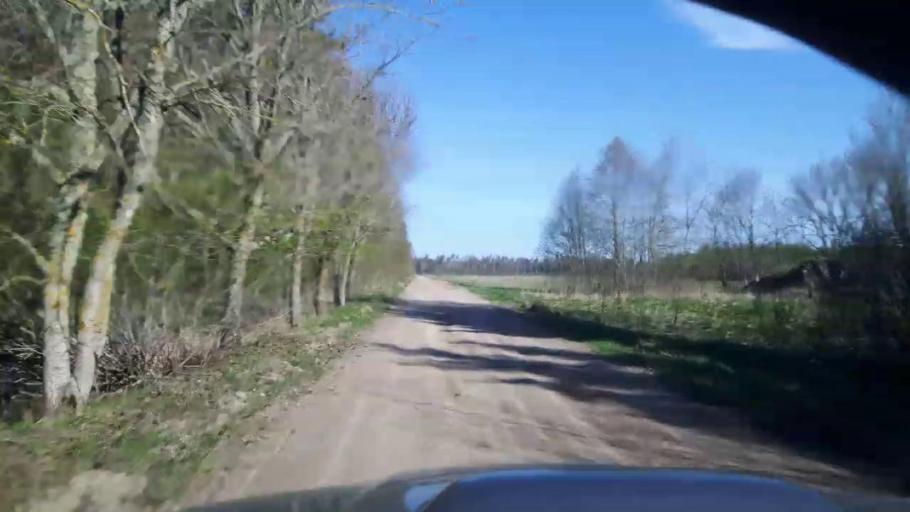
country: EE
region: Paernumaa
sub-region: Tootsi vald
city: Tootsi
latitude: 58.5072
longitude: 24.9366
